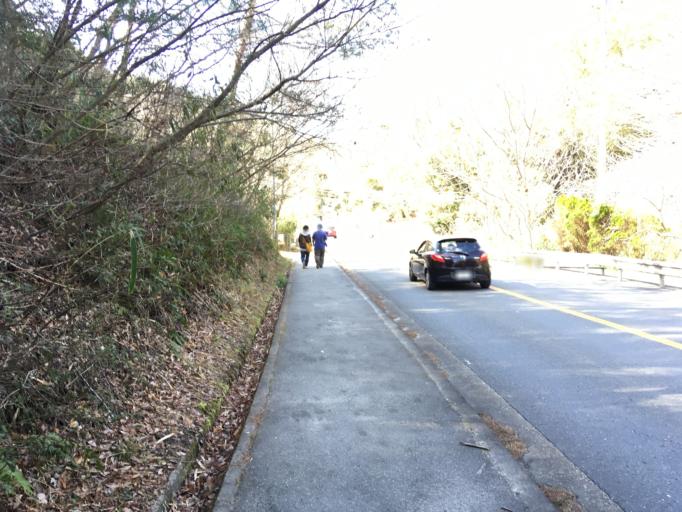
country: JP
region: Osaka
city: Neyagawa
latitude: 34.7575
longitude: 135.6901
